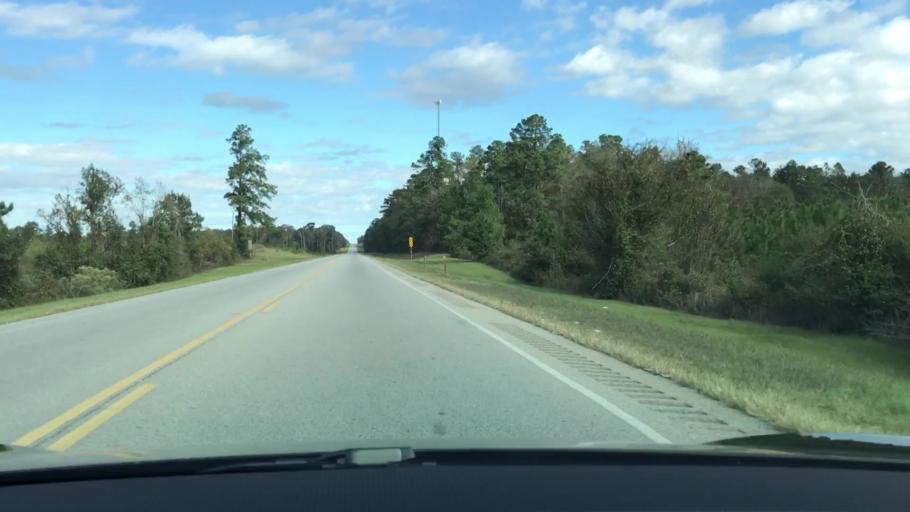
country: US
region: Georgia
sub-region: Jefferson County
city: Wadley
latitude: 32.9059
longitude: -82.3995
